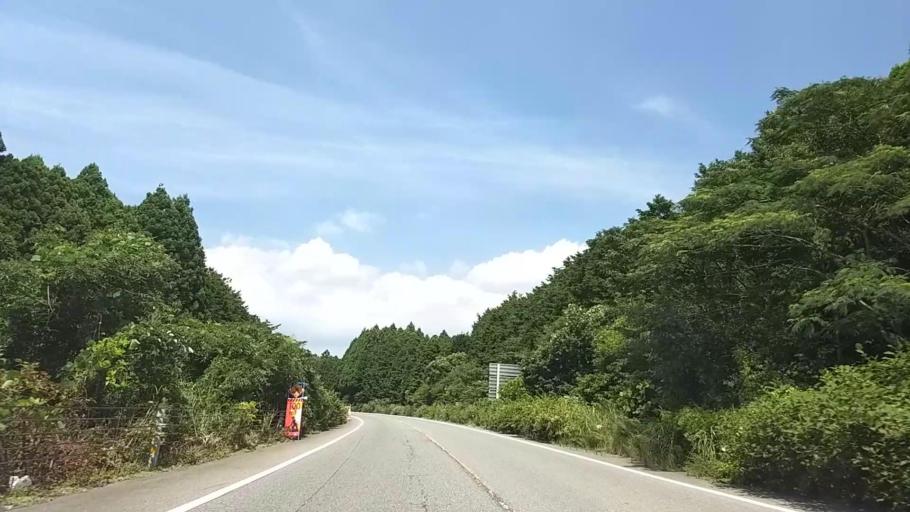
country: JP
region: Shizuoka
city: Fujinomiya
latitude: 35.3227
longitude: 138.5904
